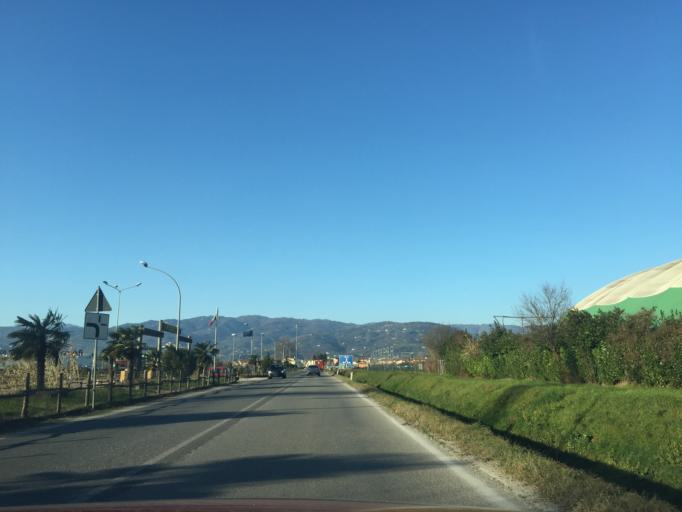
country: IT
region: Tuscany
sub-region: Provincia di Pistoia
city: Ponte Buggianese
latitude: 43.8587
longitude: 10.7673
